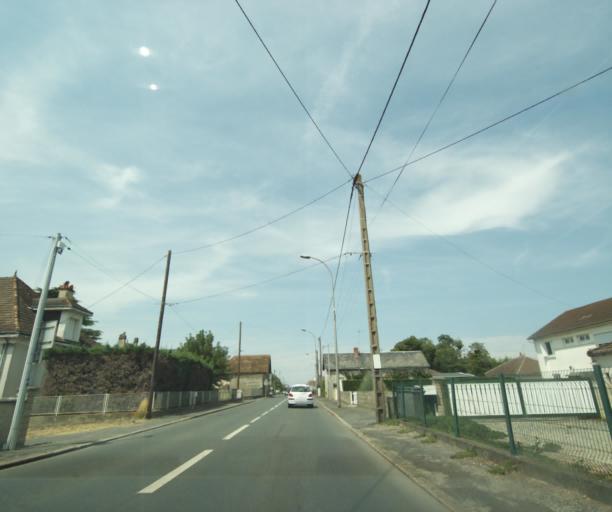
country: FR
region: Poitou-Charentes
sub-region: Departement de la Vienne
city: Dange-Saint-Romain
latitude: 46.9393
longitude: 0.6068
